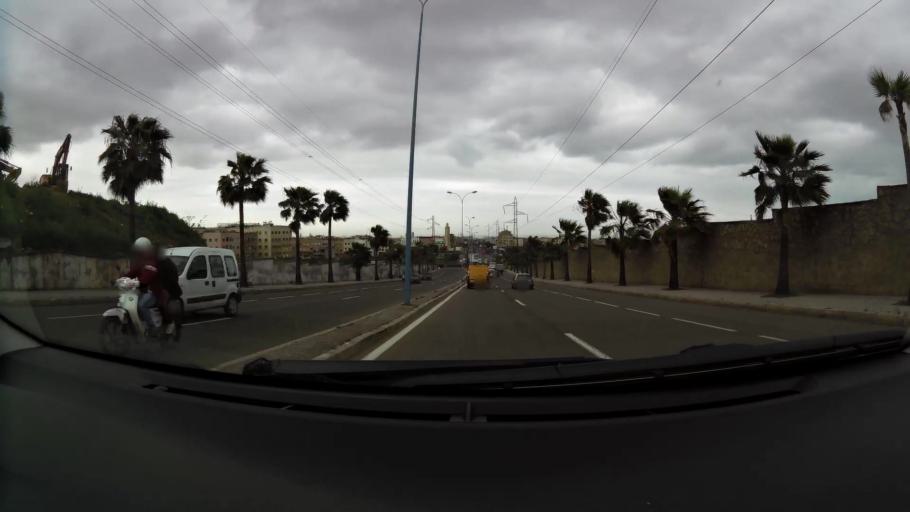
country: MA
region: Grand Casablanca
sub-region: Mediouna
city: Tit Mellil
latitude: 33.5718
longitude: -7.5357
